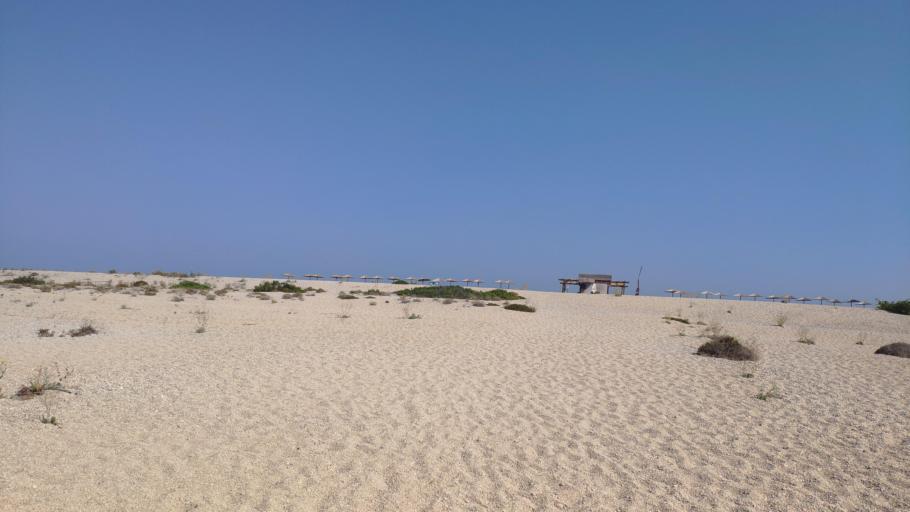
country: GR
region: Ionian Islands
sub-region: Lefkada
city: Lefkada
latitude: 38.8523
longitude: 20.7362
